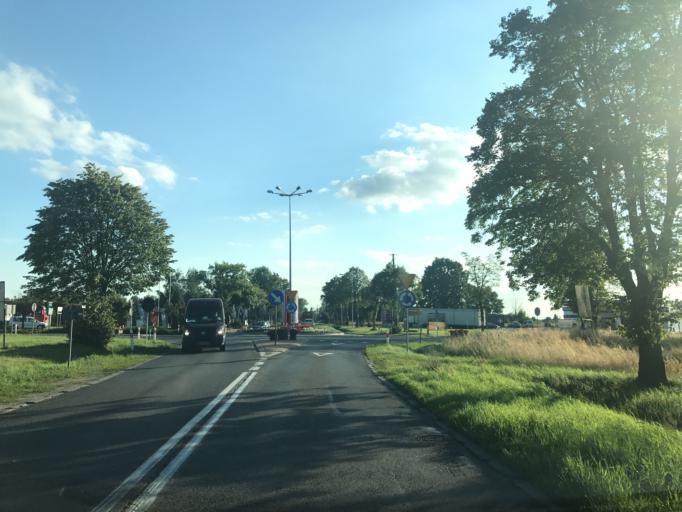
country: PL
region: Greater Poland Voivodeship
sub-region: Powiat pleszewski
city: Gizalki
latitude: 52.0459
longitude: 17.7656
